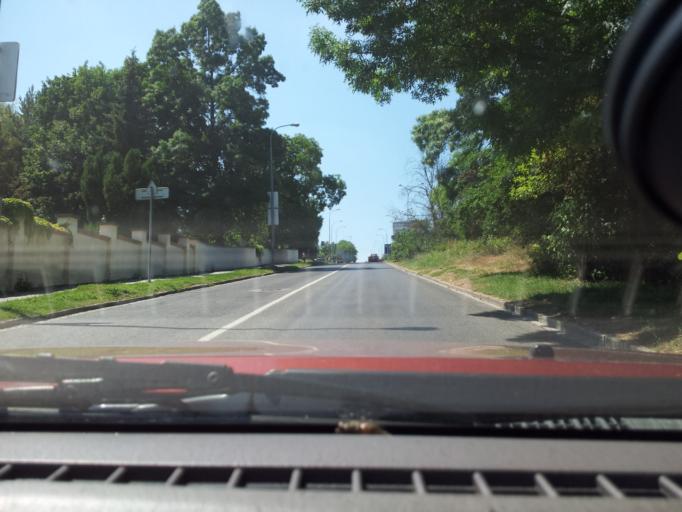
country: CZ
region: South Moravian
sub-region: Mesto Brno
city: Brno
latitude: 49.1727
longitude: 16.5928
